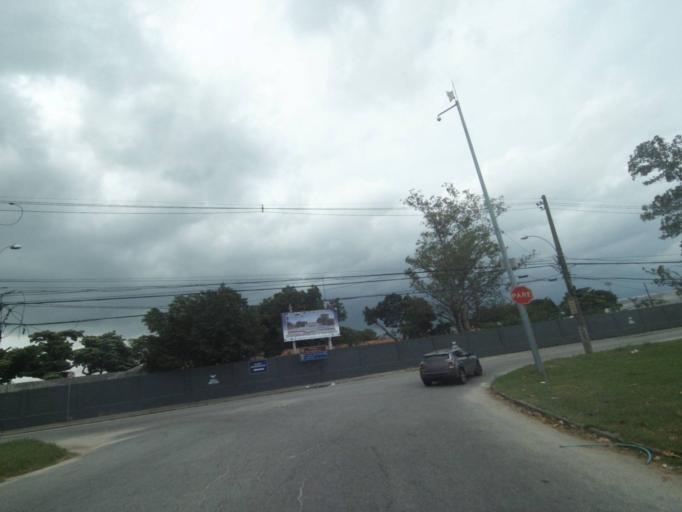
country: BR
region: Rio de Janeiro
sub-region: Nilopolis
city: Nilopolis
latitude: -22.8853
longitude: -43.3897
